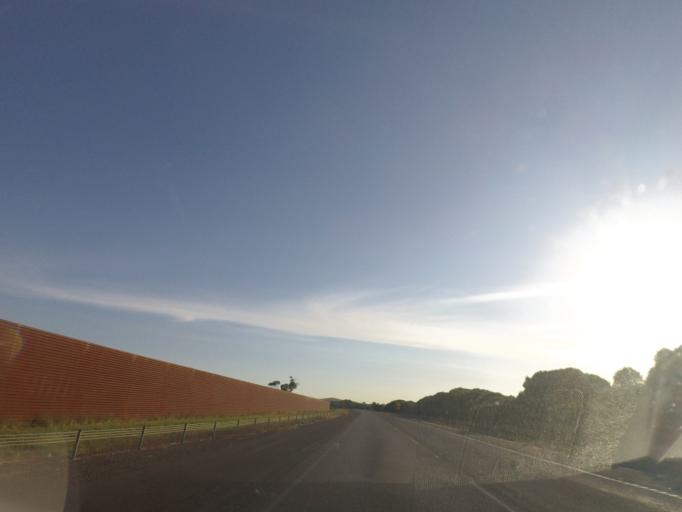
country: AU
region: Victoria
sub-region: Whittlesea
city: Whittlesea
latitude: -37.4263
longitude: 144.9871
